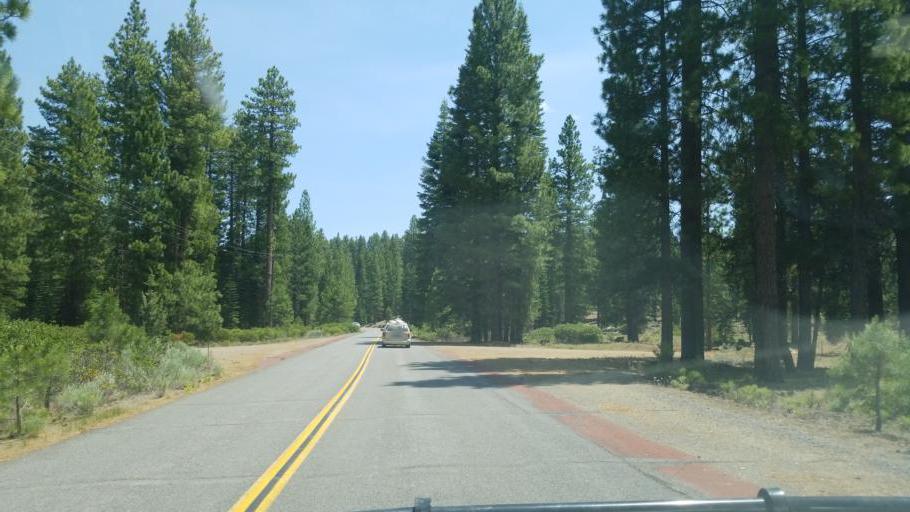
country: US
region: California
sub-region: Lassen County
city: Susanville
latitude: 40.5639
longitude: -120.8377
